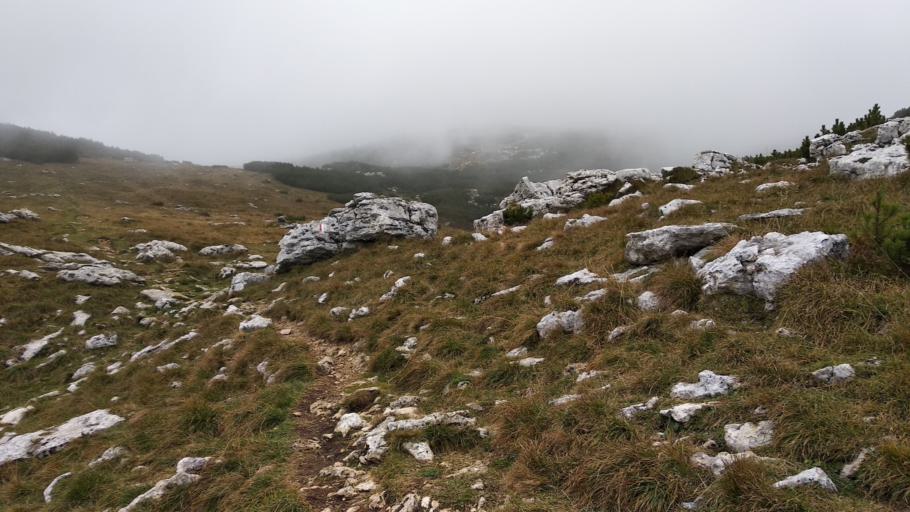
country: IT
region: Veneto
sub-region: Provincia di Vicenza
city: Roana
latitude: 45.9618
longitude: 11.4530
